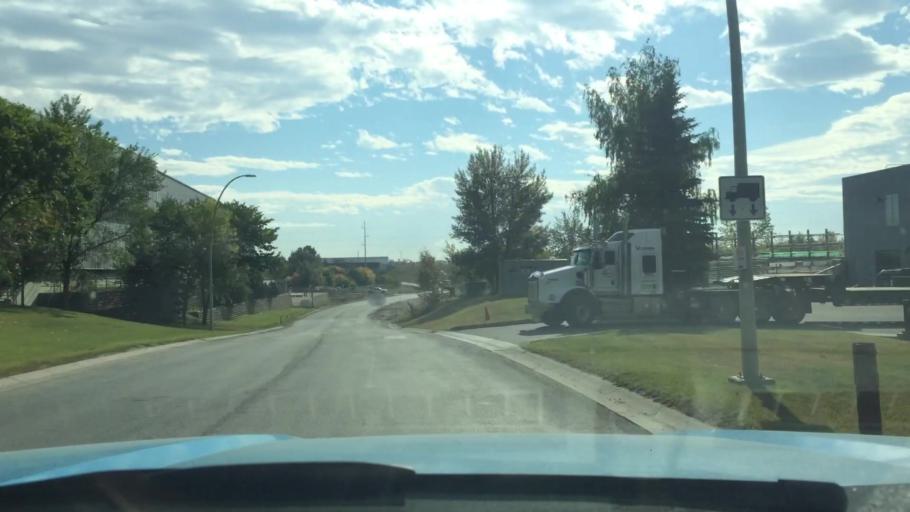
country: CA
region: Alberta
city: Calgary
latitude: 51.0090
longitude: -114.0323
